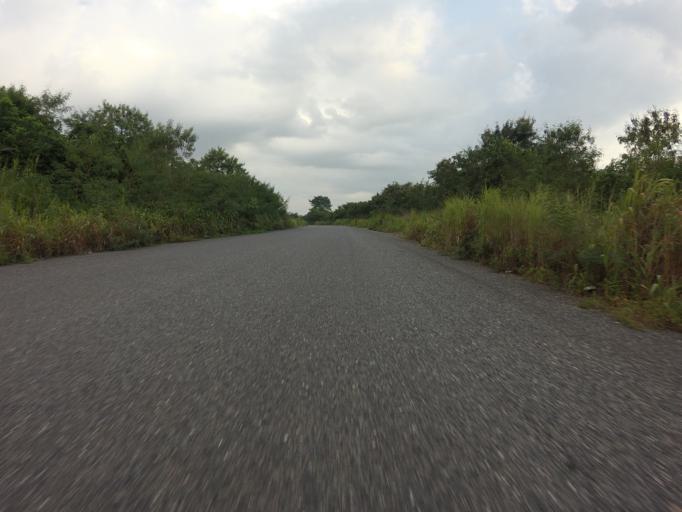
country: GH
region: Volta
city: Ho
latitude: 6.4969
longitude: 0.4870
